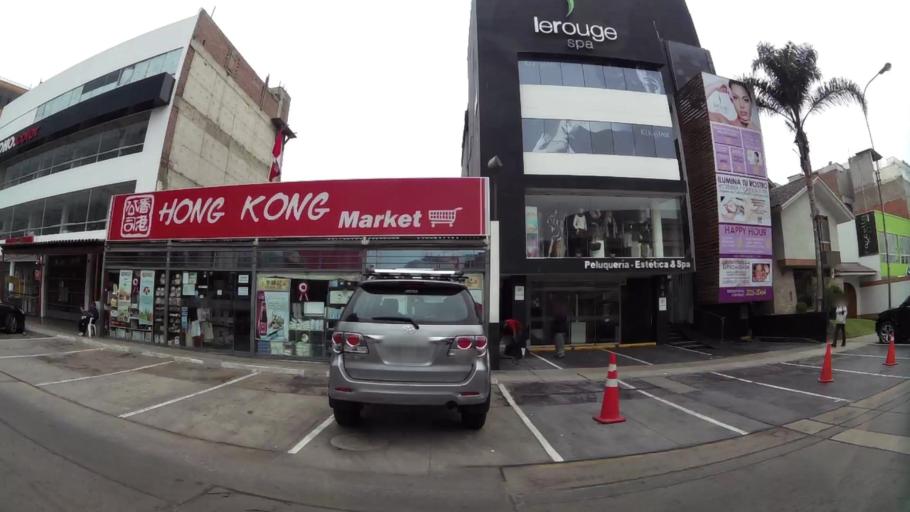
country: PE
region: Lima
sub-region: Lima
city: San Luis
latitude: -12.0913
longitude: -77.0049
